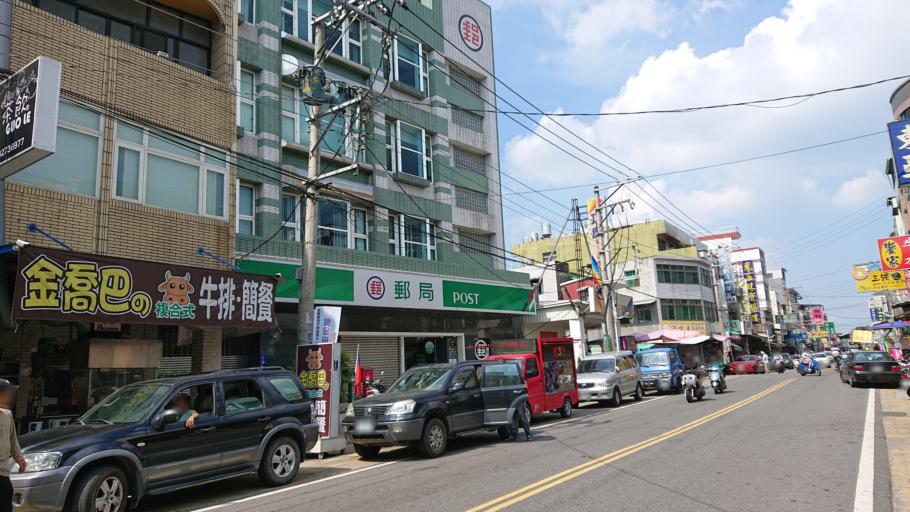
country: TW
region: Taiwan
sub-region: Nantou
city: Nantou
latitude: 23.8365
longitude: 120.7023
